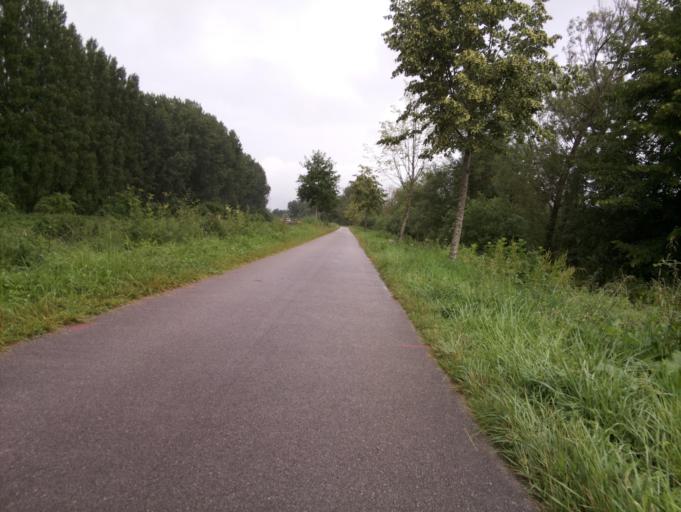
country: FR
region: Picardie
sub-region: Departement de la Somme
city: Ailly-sur-Somme
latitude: 49.9301
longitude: 2.2010
